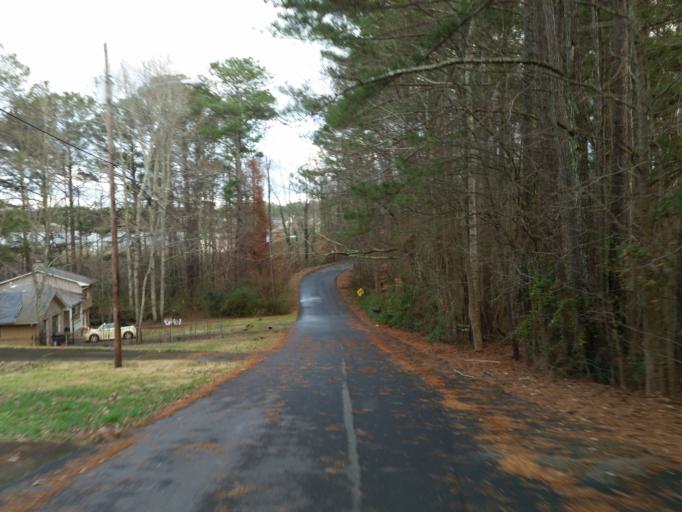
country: US
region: Georgia
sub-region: Cherokee County
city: Woodstock
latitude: 34.0401
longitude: -84.4804
